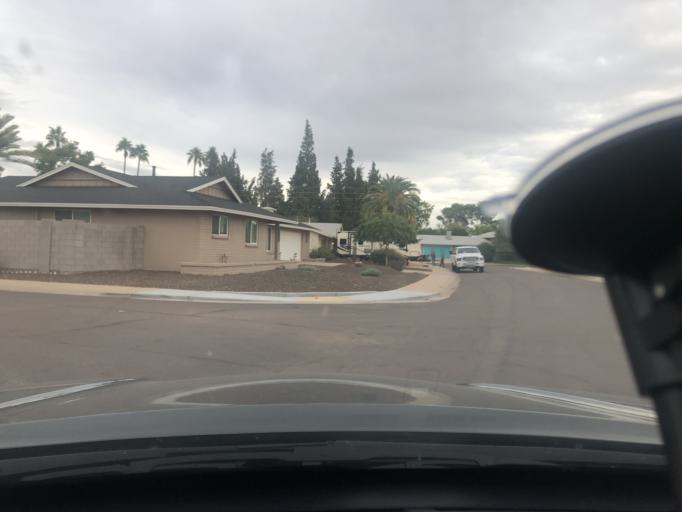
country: US
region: Arizona
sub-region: Maricopa County
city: Scottsdale
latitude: 33.4861
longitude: -111.8969
